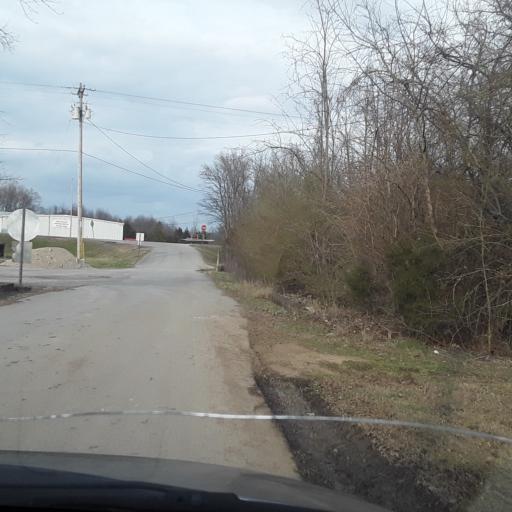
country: US
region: Tennessee
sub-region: Wilson County
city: Mount Juliet
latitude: 36.2295
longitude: -86.4262
